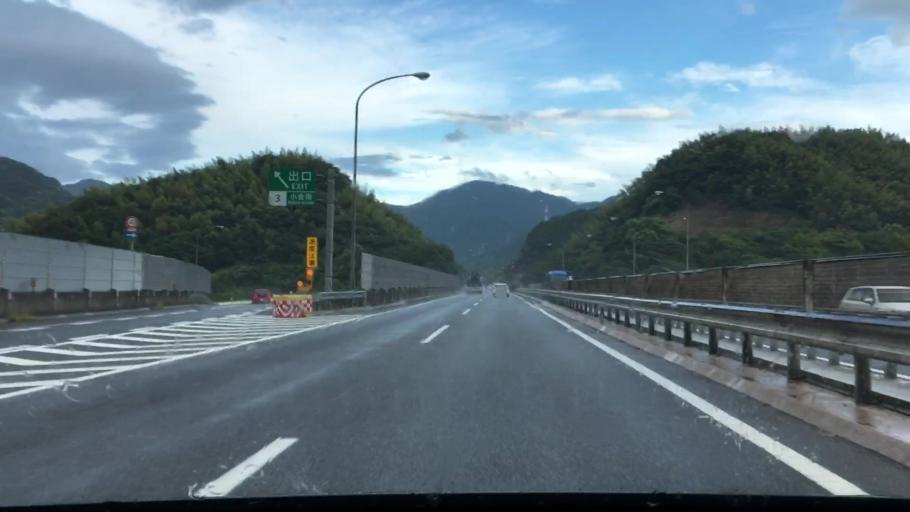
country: JP
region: Fukuoka
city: Kitakyushu
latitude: 33.8044
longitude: 130.8513
